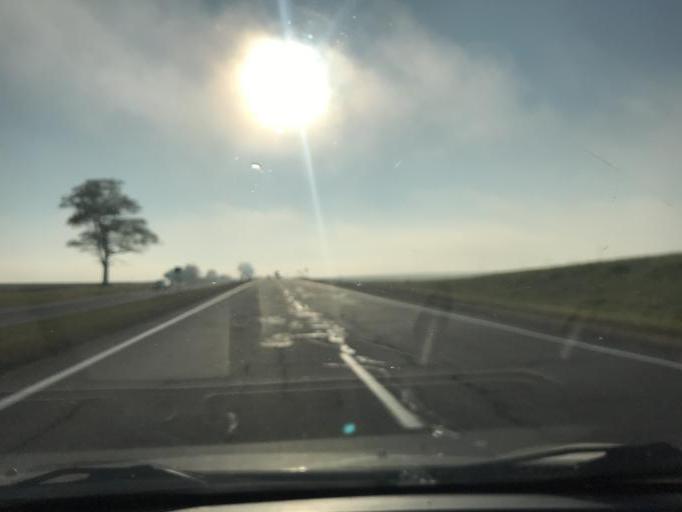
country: BY
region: Minsk
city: Dukora
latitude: 53.6862
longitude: 27.9118
